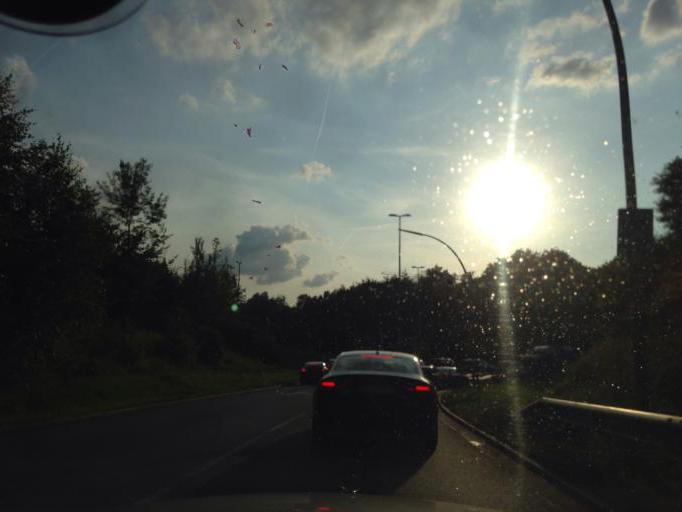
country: DE
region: Hamburg
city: Wandsbek
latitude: 53.5672
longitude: 10.1240
